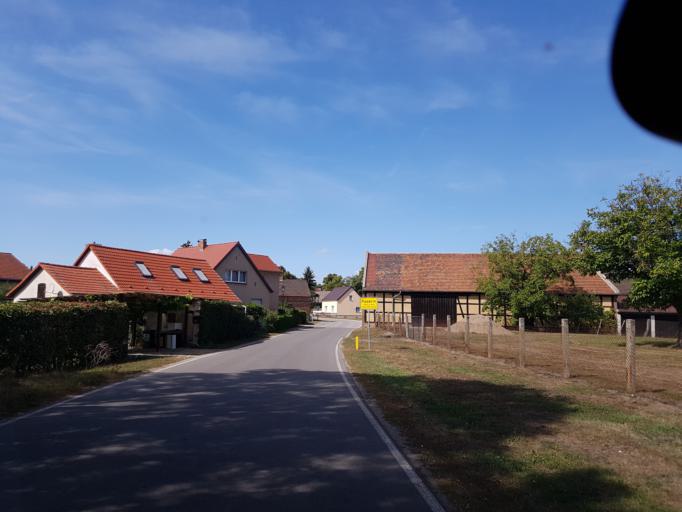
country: DE
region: Brandenburg
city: Drahnsdorf
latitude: 51.8590
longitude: 13.6280
